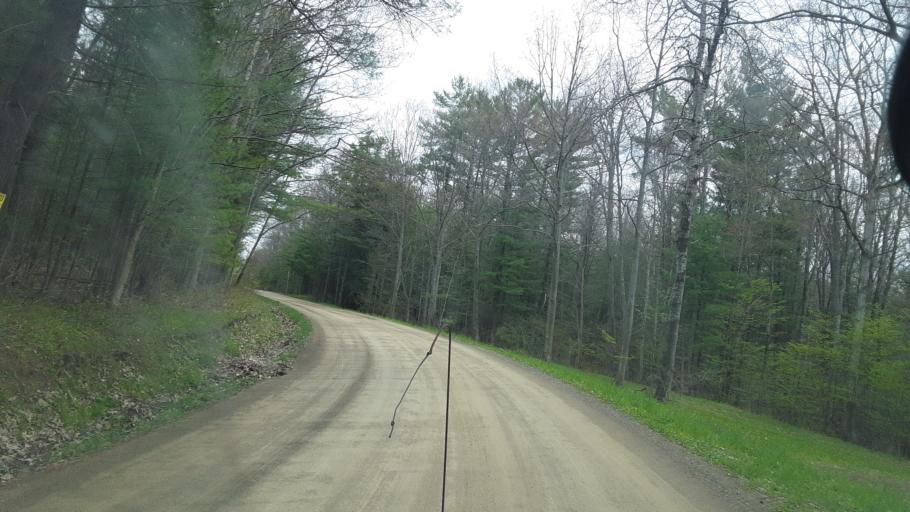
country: US
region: New York
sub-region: Steuben County
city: Addison
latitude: 42.0937
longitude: -77.3193
